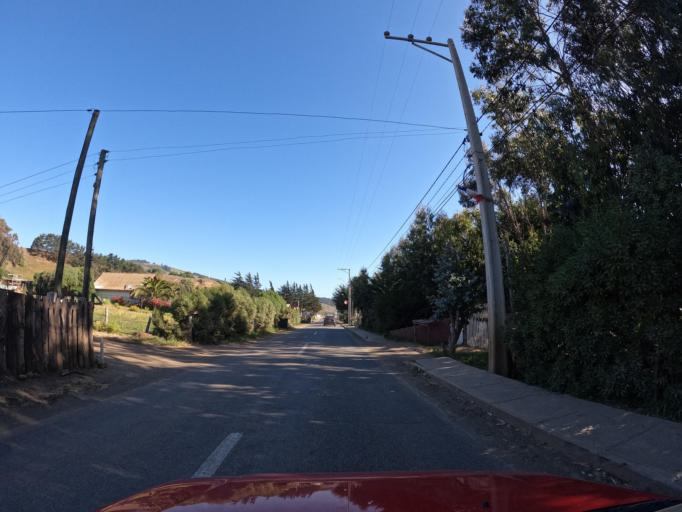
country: CL
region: Maule
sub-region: Provincia de Talca
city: Constitucion
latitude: -34.8482
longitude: -72.1413
